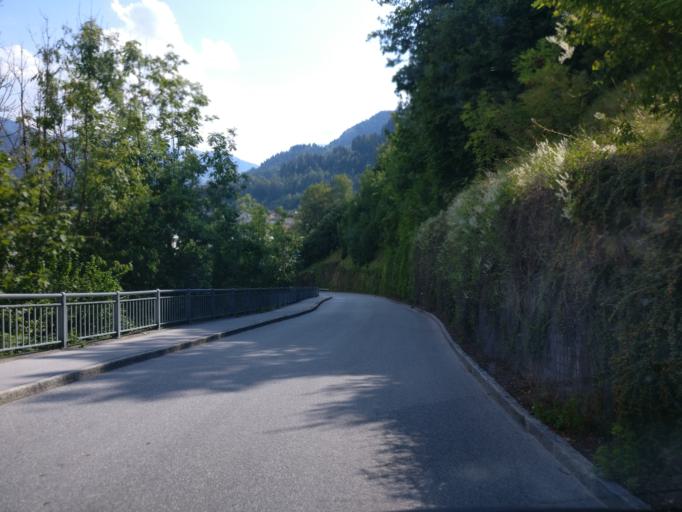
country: AT
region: Salzburg
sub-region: Politischer Bezirk Sankt Johann im Pongau
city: Bischofshofen
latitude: 47.4133
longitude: 13.2155
